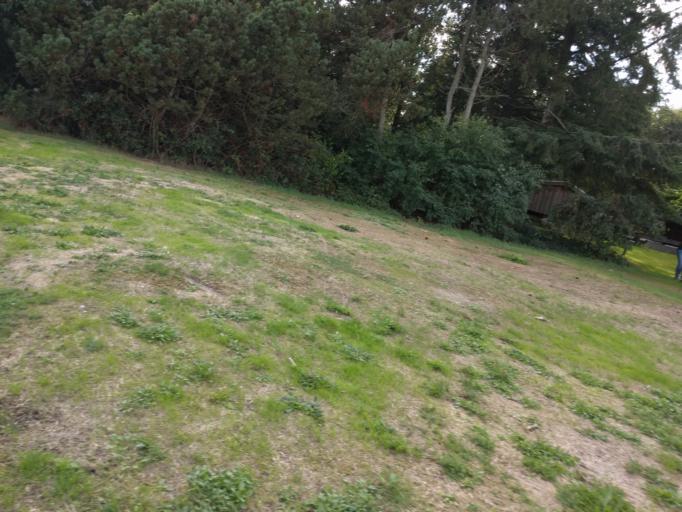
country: DK
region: Central Jutland
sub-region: Skive Kommune
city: Hojslev
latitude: 56.6028
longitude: 9.2866
